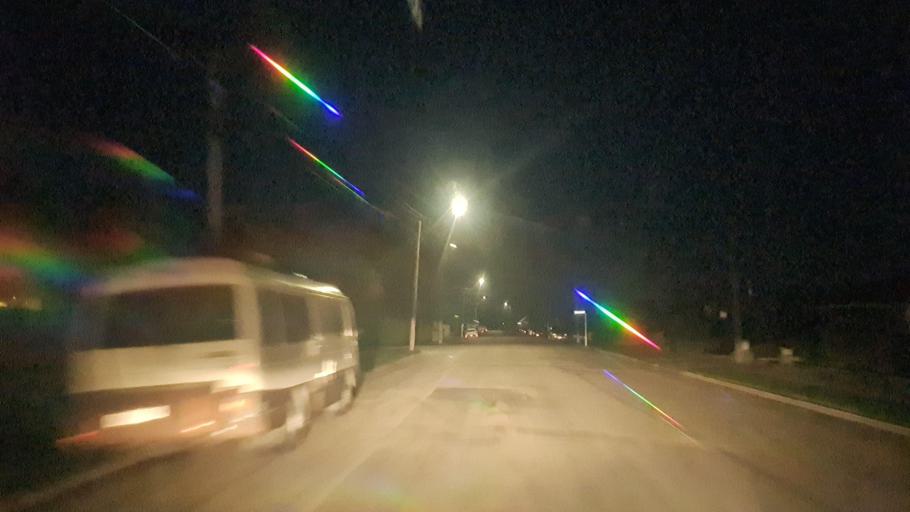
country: NZ
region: Otago
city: Oamaru
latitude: -45.0692
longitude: 170.9882
